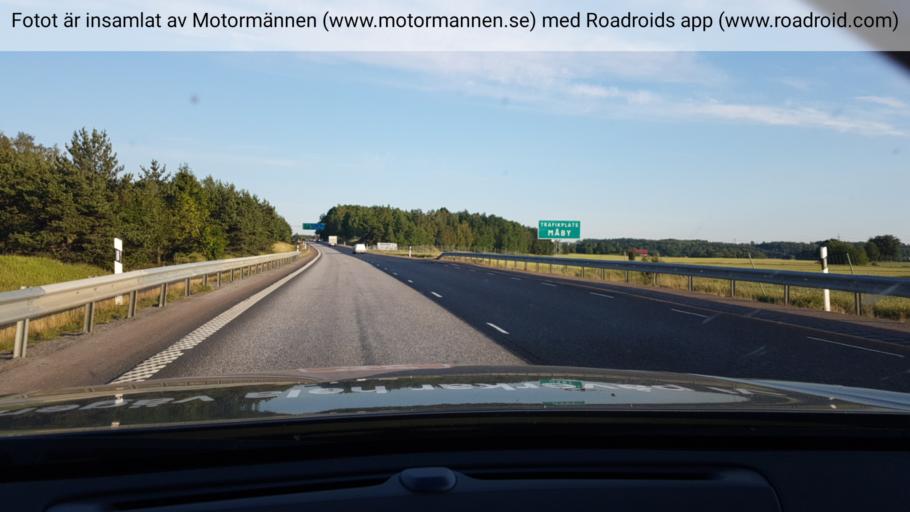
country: SE
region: Stockholm
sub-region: Sigtuna Kommun
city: Marsta
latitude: 59.6429
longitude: 17.8921
